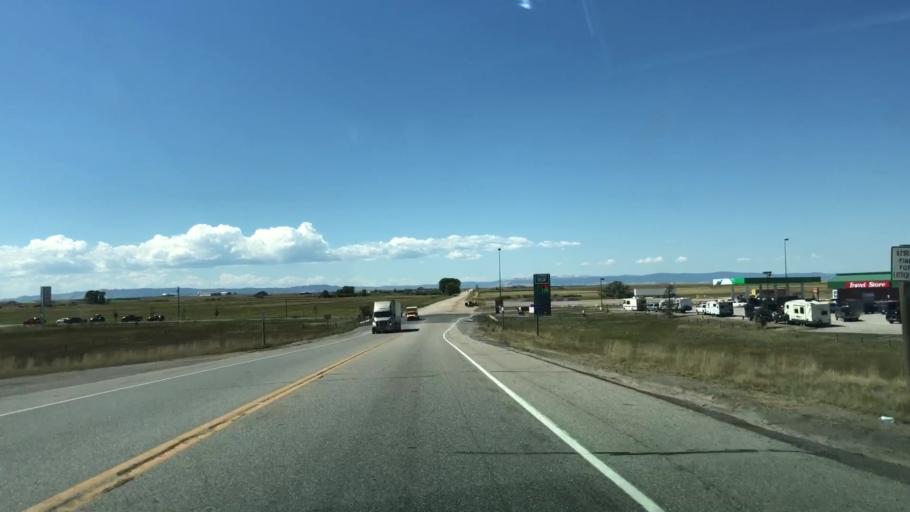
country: US
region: Wyoming
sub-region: Albany County
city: Laramie
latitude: 41.3279
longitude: -105.6175
